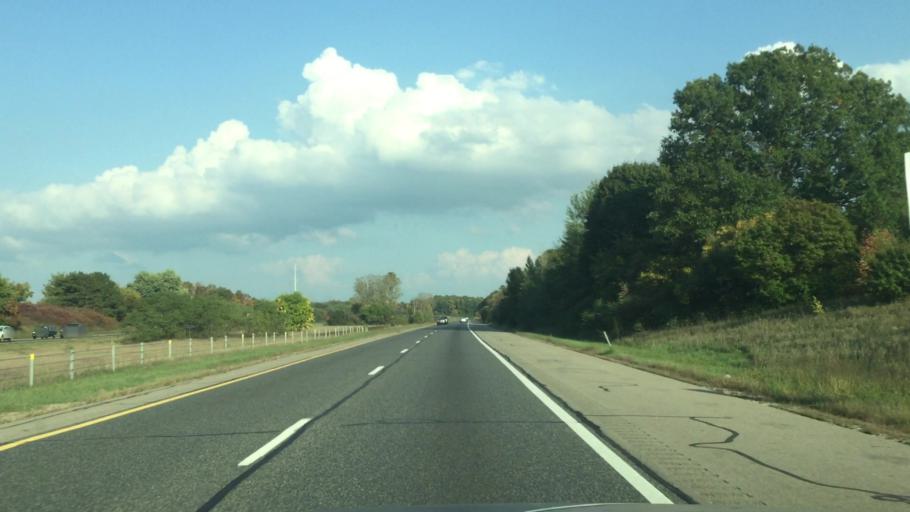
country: US
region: Michigan
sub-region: Washtenaw County
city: Chelsea
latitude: 42.2987
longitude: -83.9580
